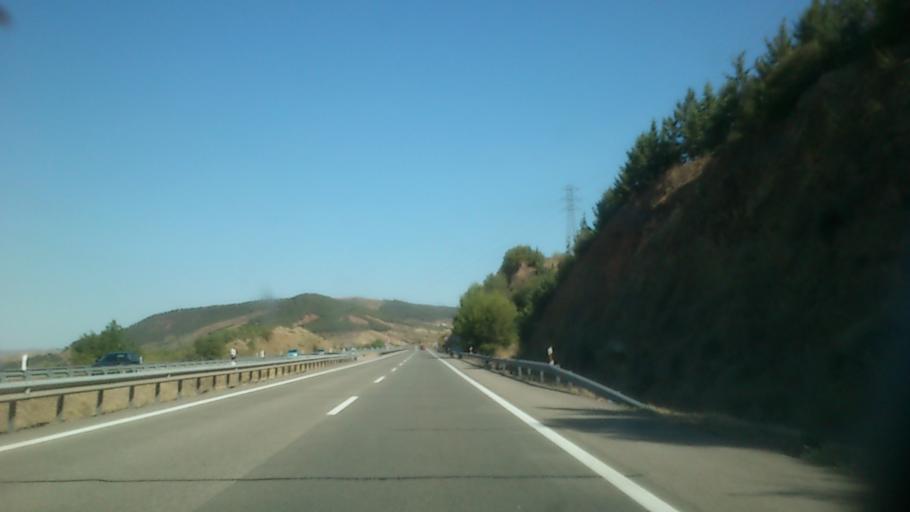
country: ES
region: Aragon
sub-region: Provincia de Zaragoza
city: Ateca
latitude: 41.3132
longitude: -1.7689
